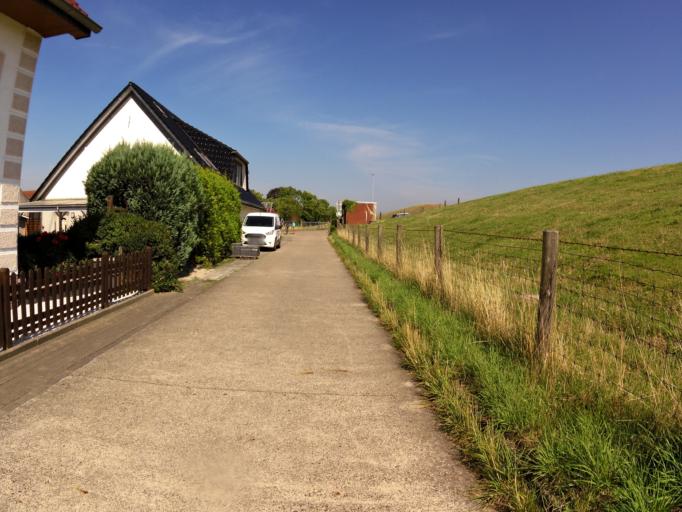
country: DE
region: Lower Saxony
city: Elsfleth
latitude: 53.2763
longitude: 8.4808
